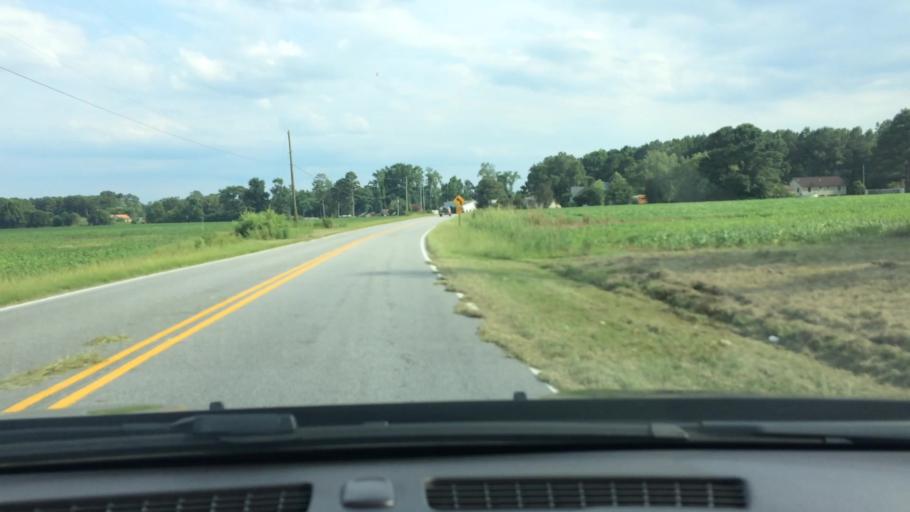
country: US
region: North Carolina
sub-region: Pitt County
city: Winterville
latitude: 35.4953
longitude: -77.3784
